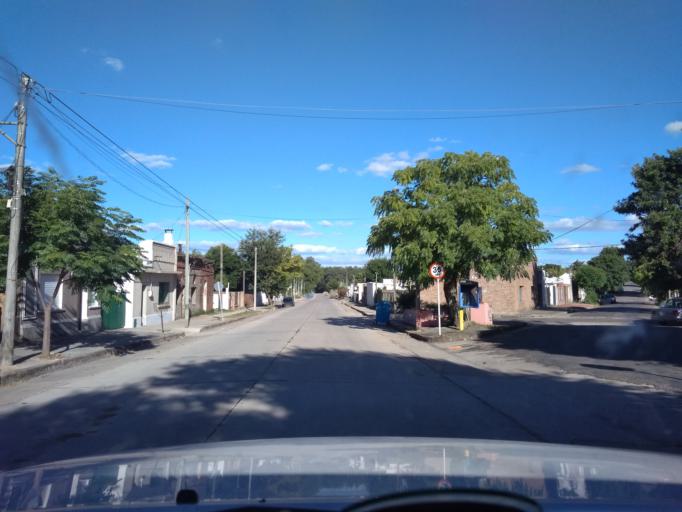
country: UY
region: Florida
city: Florida
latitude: -34.0919
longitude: -56.2128
